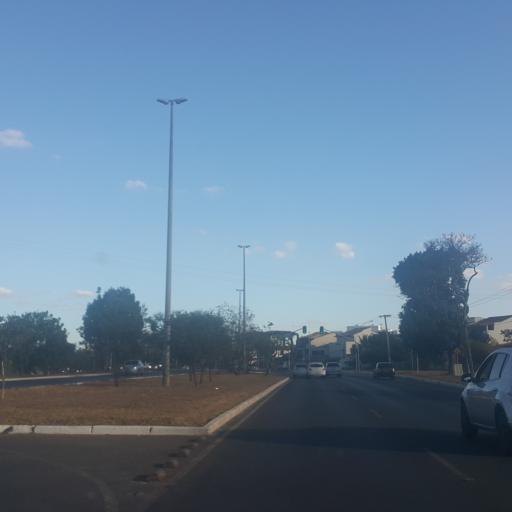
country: BR
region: Federal District
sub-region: Brasilia
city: Brasilia
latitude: -15.8328
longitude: -47.9748
